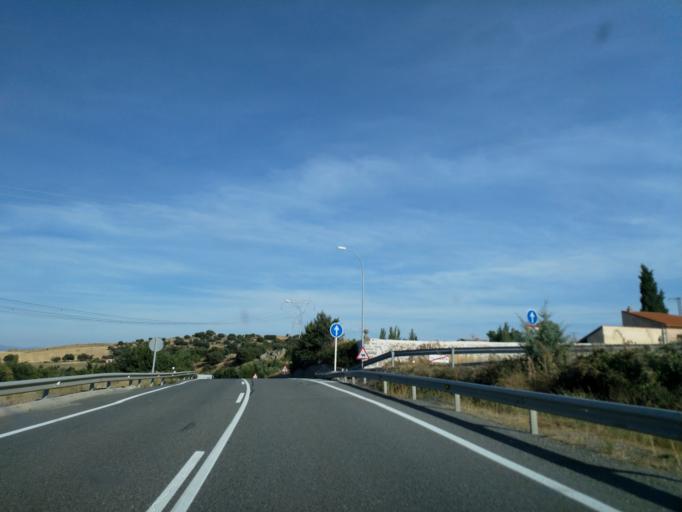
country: ES
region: Castille and Leon
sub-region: Provincia de Segovia
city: Villacastin
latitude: 40.7829
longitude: -4.4120
